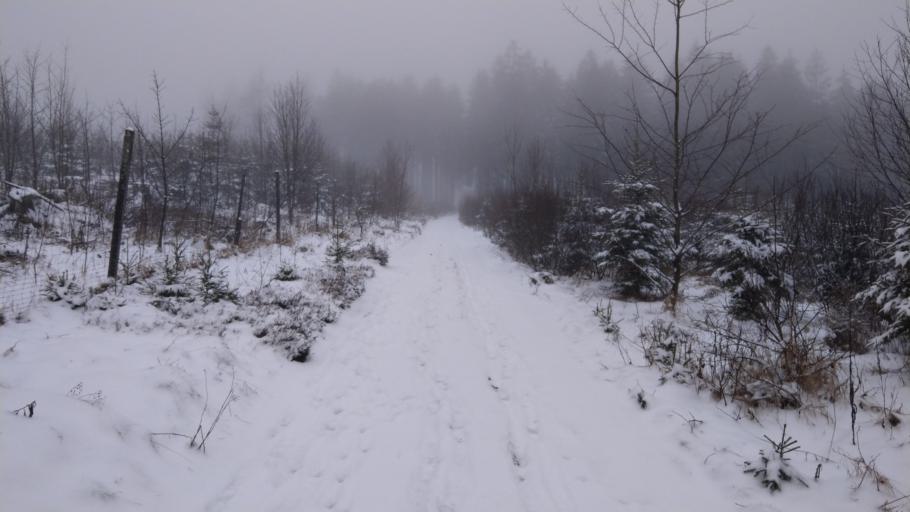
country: DE
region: North Rhine-Westphalia
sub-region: Regierungsbezirk Arnsberg
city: Erndtebruck
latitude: 50.9844
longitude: 8.2169
